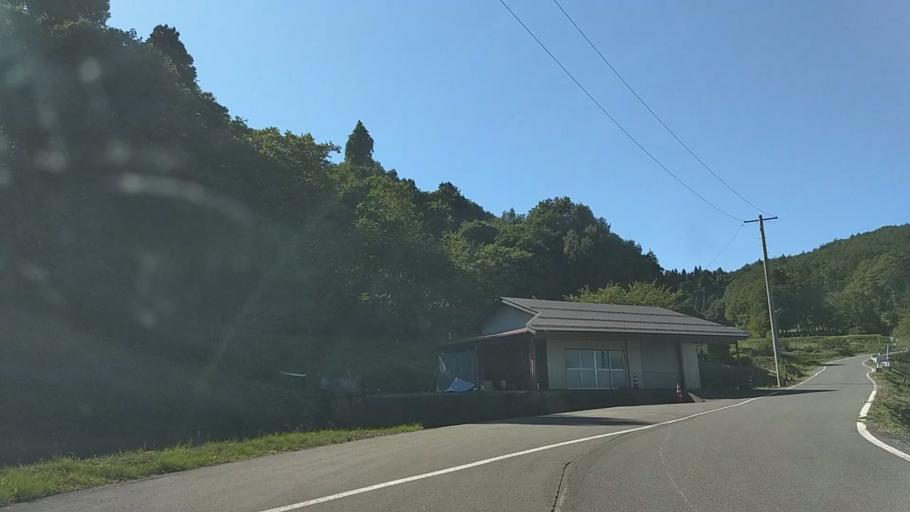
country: JP
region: Nagano
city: Nagano-shi
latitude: 36.5820
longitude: 138.1005
